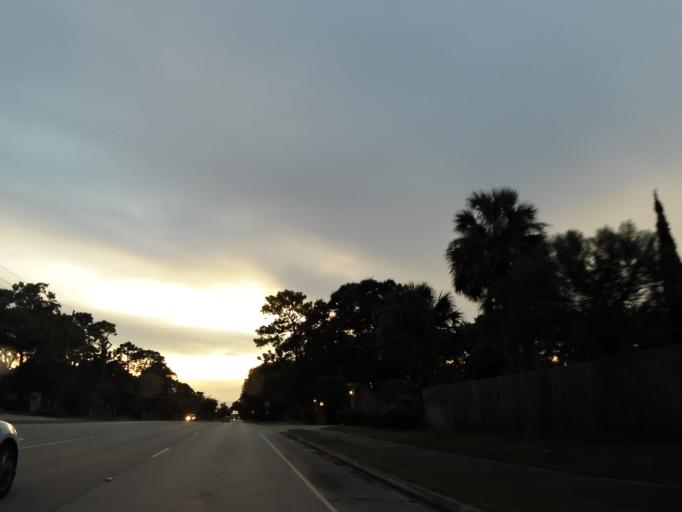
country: US
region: Florida
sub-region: Duval County
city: Jacksonville
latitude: 30.3666
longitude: -81.5819
